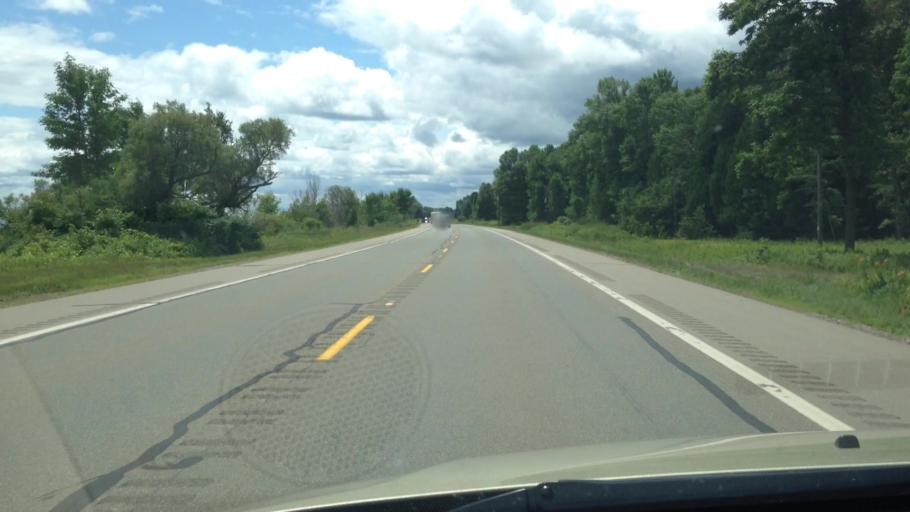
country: US
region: Michigan
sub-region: Menominee County
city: Menominee
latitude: 45.2542
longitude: -87.4841
